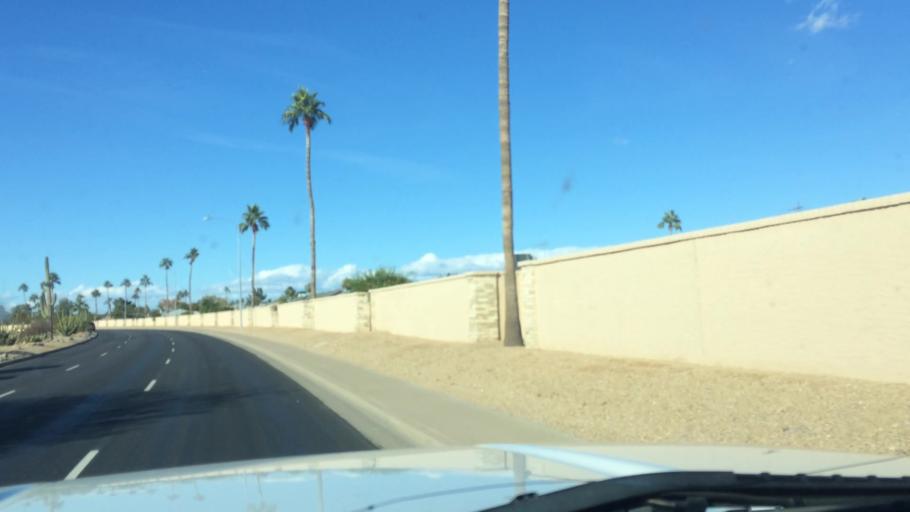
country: US
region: Arizona
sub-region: Maricopa County
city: Surprise
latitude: 33.6449
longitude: -112.3345
